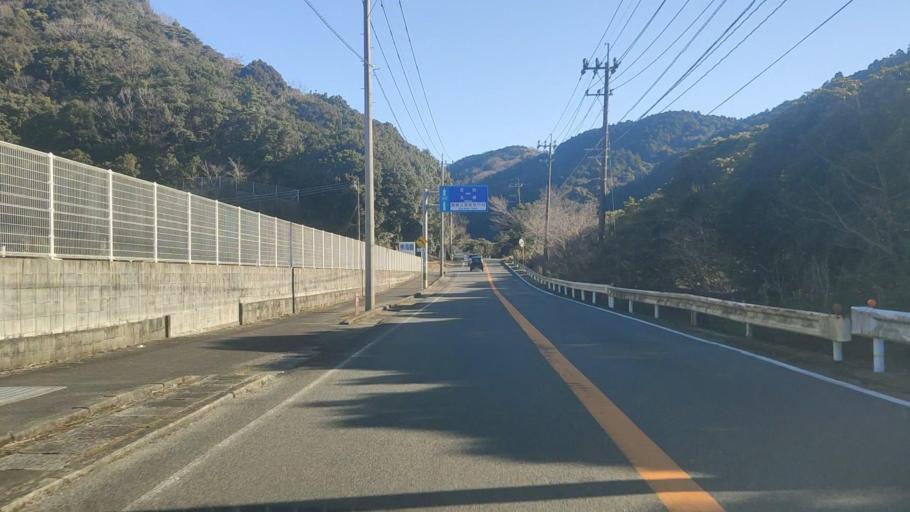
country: JP
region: Miyazaki
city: Nobeoka
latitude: 32.6186
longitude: 131.7023
